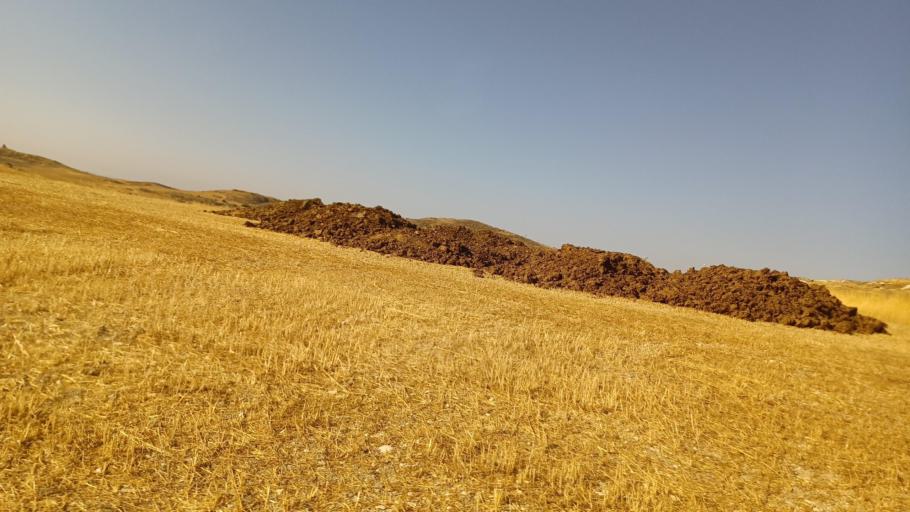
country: CY
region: Larnaka
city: Troulloi
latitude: 35.0260
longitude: 33.5781
